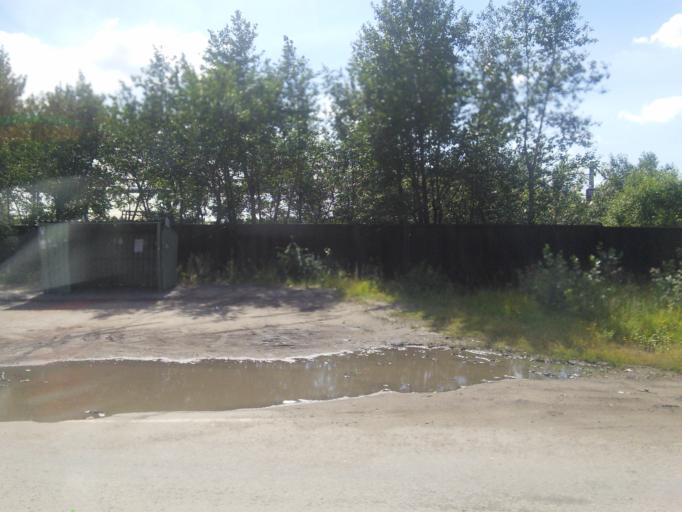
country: RU
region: Vologda
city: Cherepovets
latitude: 59.1538
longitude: 37.8605
